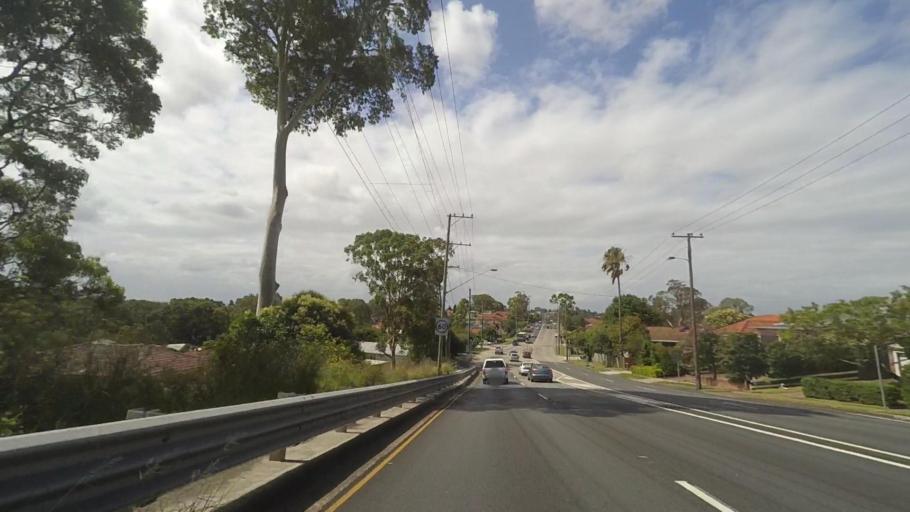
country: AU
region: New South Wales
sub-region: Newcastle
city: Lambton
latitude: -32.9180
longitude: 151.7034
